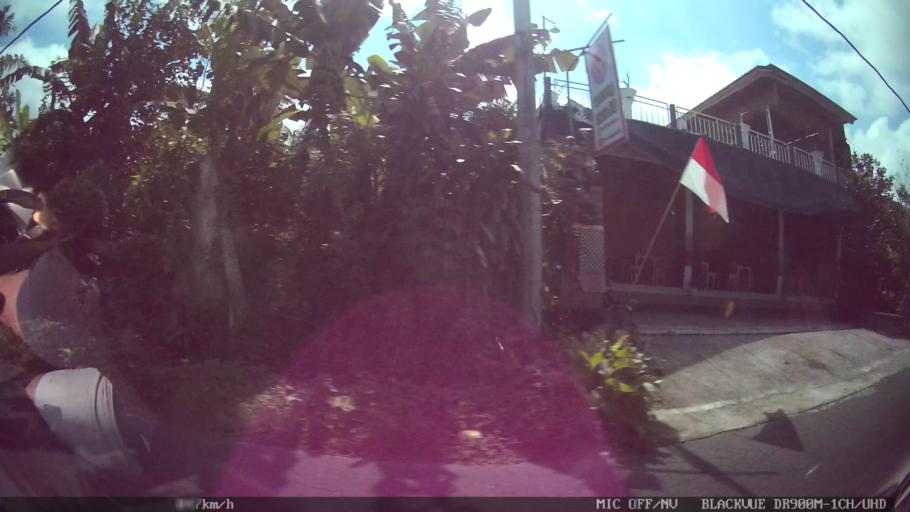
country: ID
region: Bali
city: Banjar Kelodan
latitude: -8.5230
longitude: 115.3294
